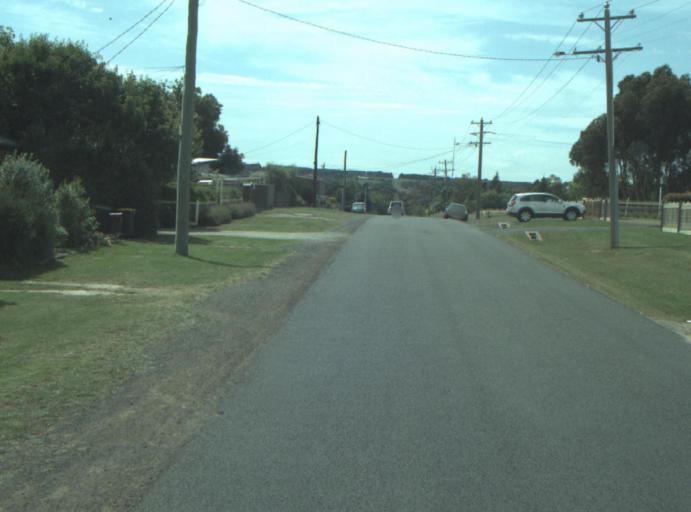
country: AU
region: Victoria
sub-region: Greater Geelong
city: Clifton Springs
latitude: -38.1587
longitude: 144.5746
